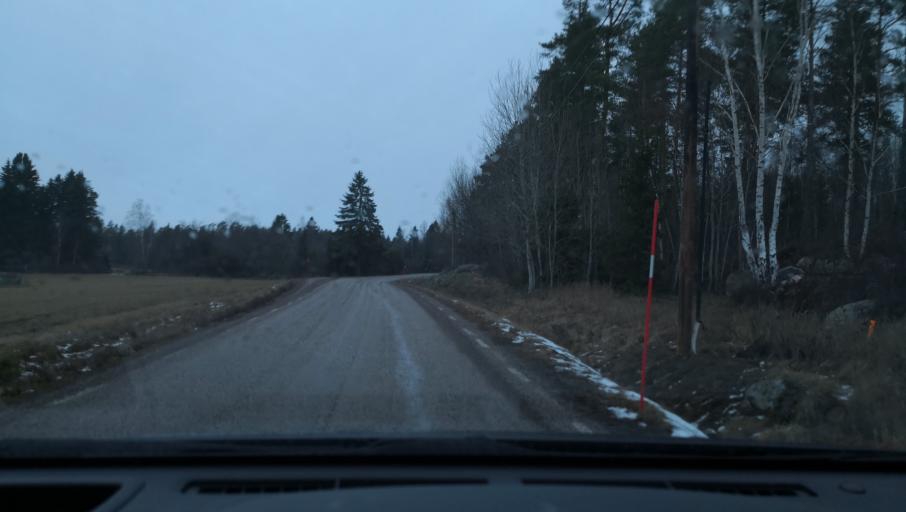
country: SE
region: Uppsala
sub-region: Enkopings Kommun
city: Hummelsta
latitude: 59.4579
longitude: 16.8478
